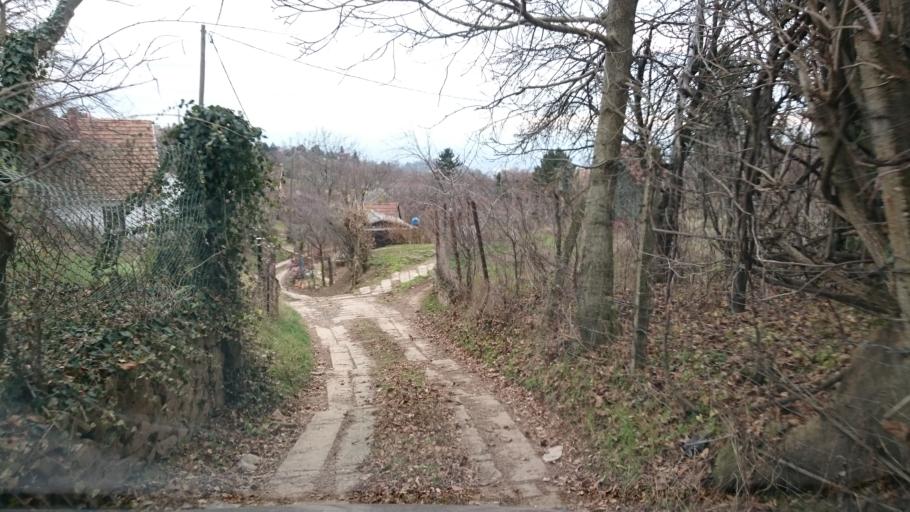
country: HU
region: Baranya
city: Pellerd
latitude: 46.0800
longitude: 18.1776
